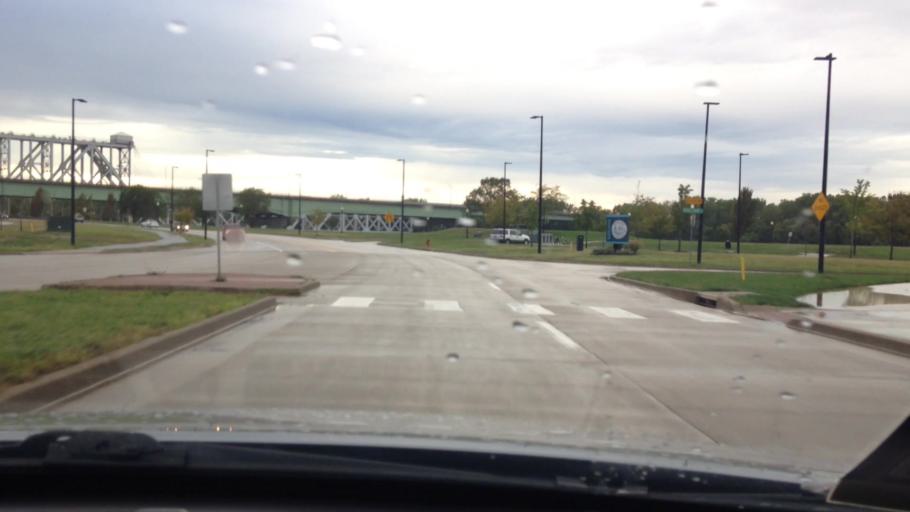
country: US
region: Missouri
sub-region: Jackson County
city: Kansas City
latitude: 39.1154
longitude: -94.5740
